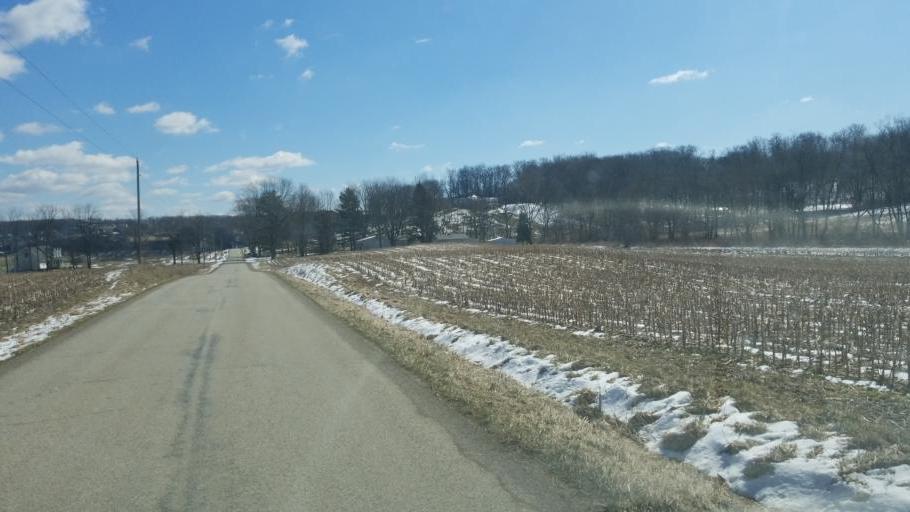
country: US
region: Ohio
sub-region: Sandusky County
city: Bellville
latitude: 40.6044
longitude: -82.5272
